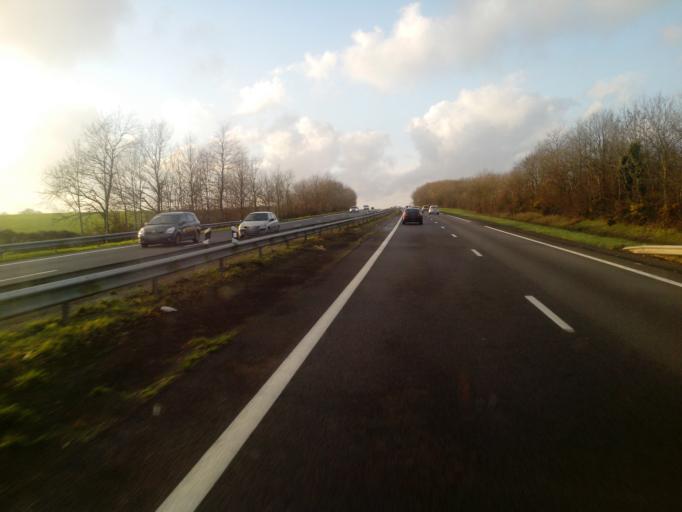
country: FR
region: Pays de la Loire
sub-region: Departement de Maine-et-Loire
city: Saint-Germain-sur-Moine
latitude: 47.1294
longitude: -1.1280
